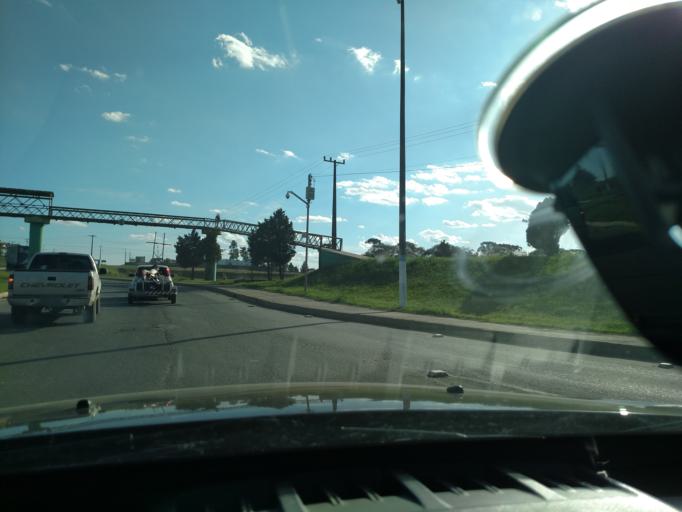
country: BR
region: Santa Catarina
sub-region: Otacilio Costa
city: Otacilio Costa
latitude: -27.4995
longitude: -50.1240
